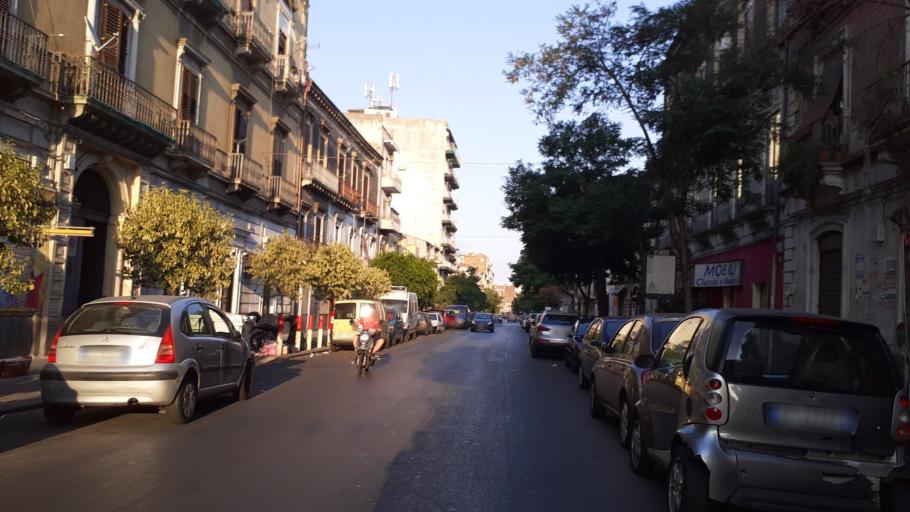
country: IT
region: Sicily
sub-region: Catania
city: Catania
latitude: 37.4986
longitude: 15.0804
